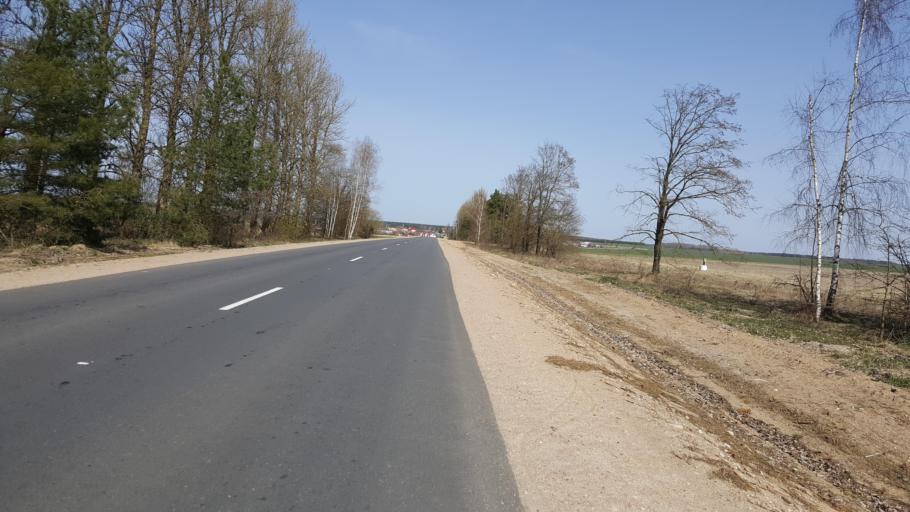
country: BY
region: Brest
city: Kamyanyets
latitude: 52.4558
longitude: 23.7354
